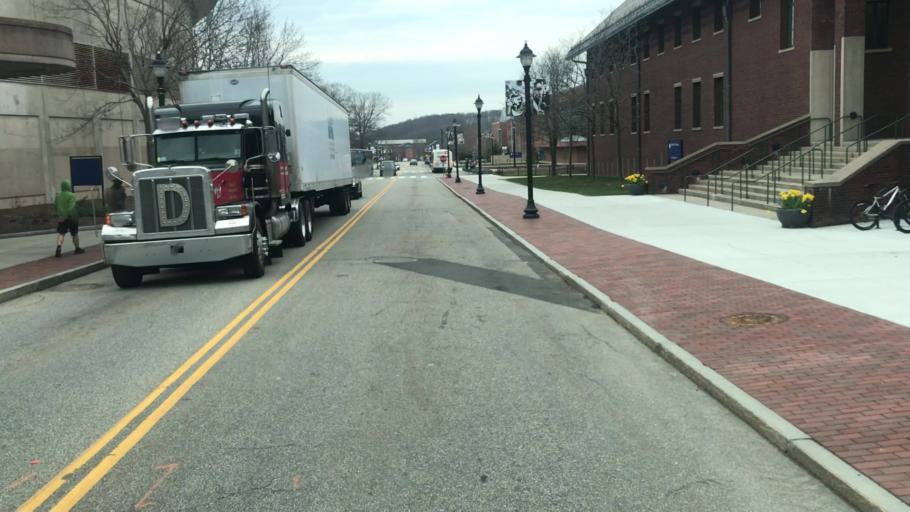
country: US
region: Connecticut
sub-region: Tolland County
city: Storrs
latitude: 41.8053
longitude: -72.2535
